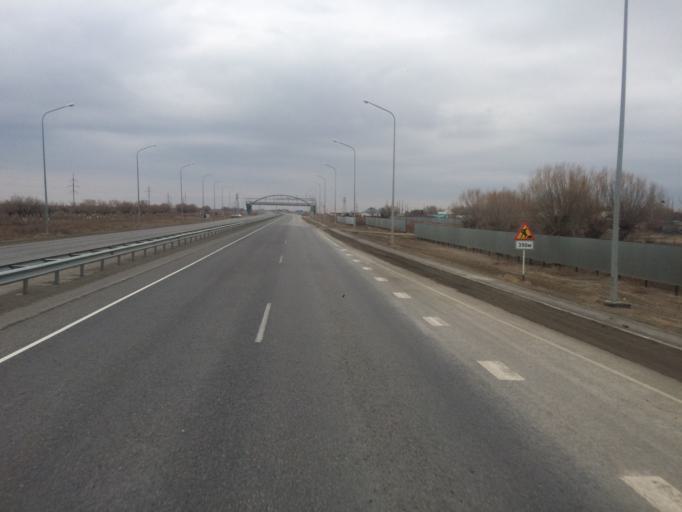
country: KZ
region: Qyzylorda
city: Shieli
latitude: 44.1360
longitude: 66.9715
